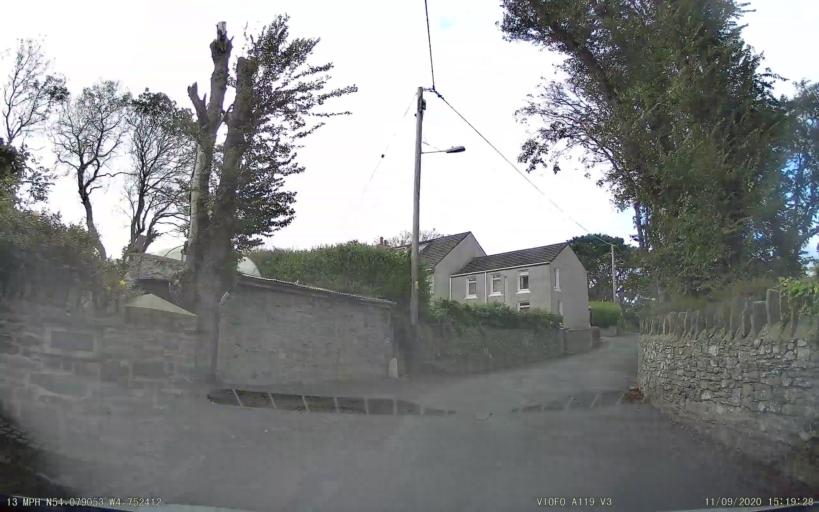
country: IM
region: Port Erin
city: Port Erin
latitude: 54.0790
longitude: -4.7524
